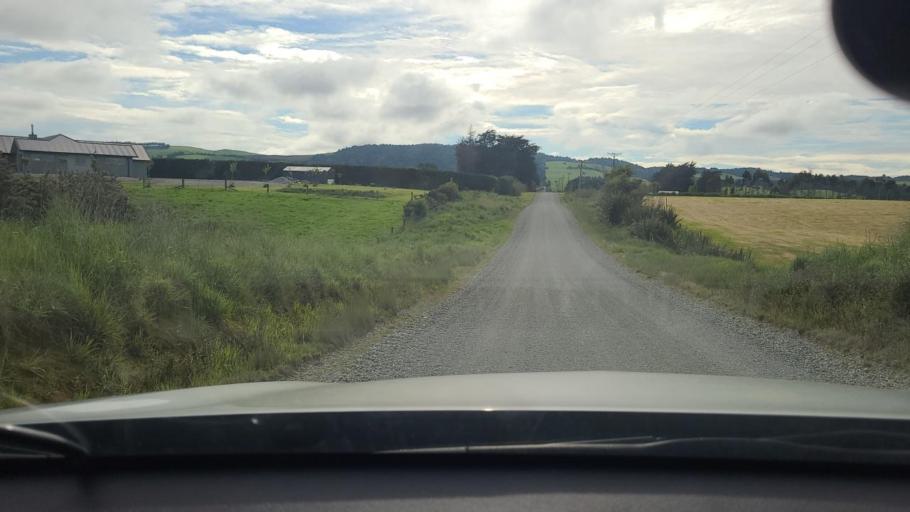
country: NZ
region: Southland
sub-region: Southland District
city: Winton
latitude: -46.2050
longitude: 168.4006
